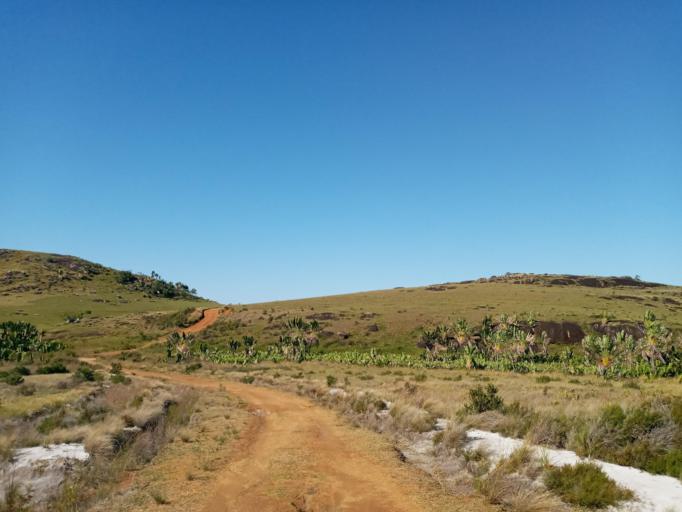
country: MG
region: Anosy
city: Fort Dauphin
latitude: -24.9117
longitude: 47.0794
